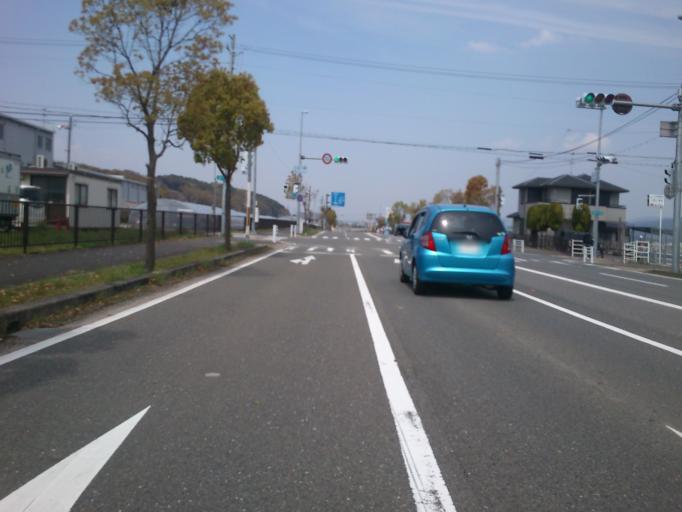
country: JP
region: Kyoto
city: Tanabe
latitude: 34.7655
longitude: 135.7876
